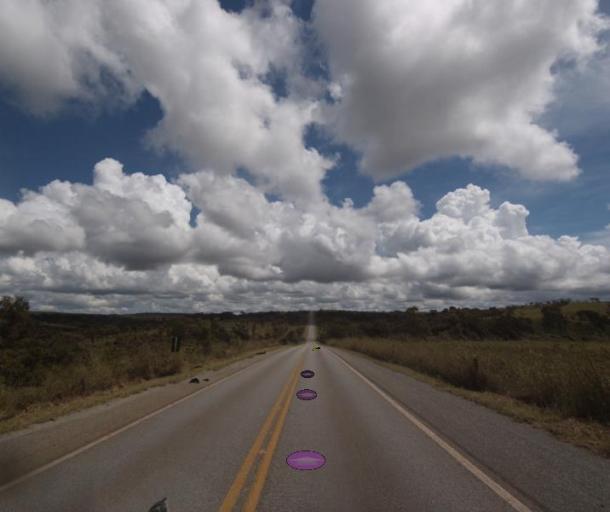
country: BR
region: Goias
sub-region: Pirenopolis
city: Pirenopolis
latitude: -15.7508
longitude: -48.6248
